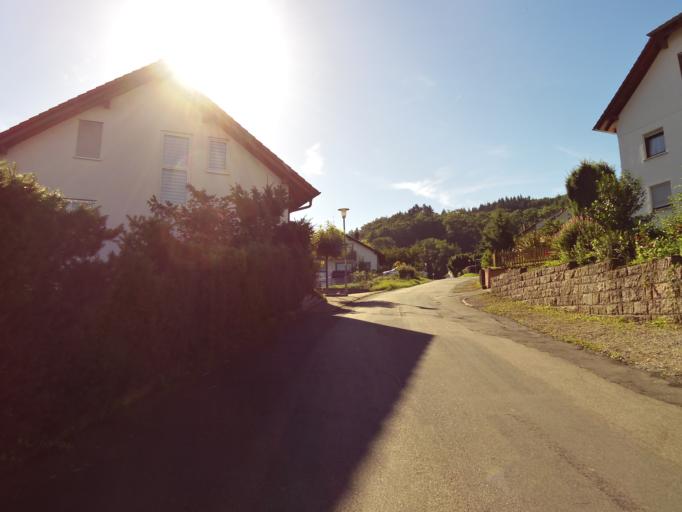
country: DE
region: Hesse
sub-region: Regierungsbezirk Darmstadt
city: Morlenbach
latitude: 49.5872
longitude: 8.7603
